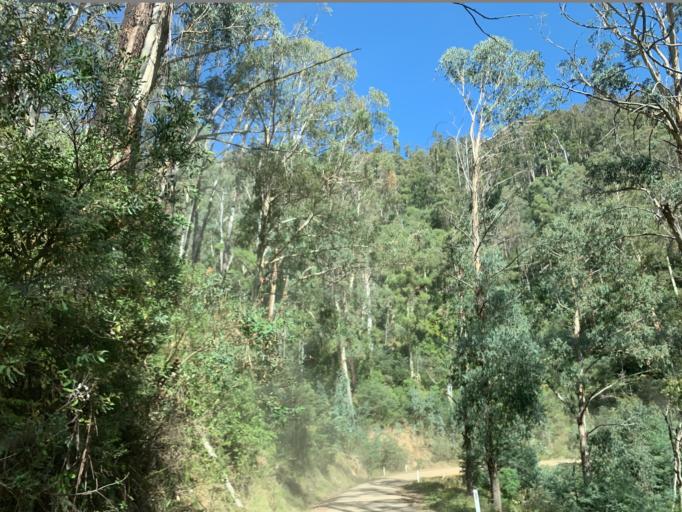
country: AU
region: Victoria
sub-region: Mansfield
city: Mansfield
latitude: -37.1014
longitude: 146.5039
